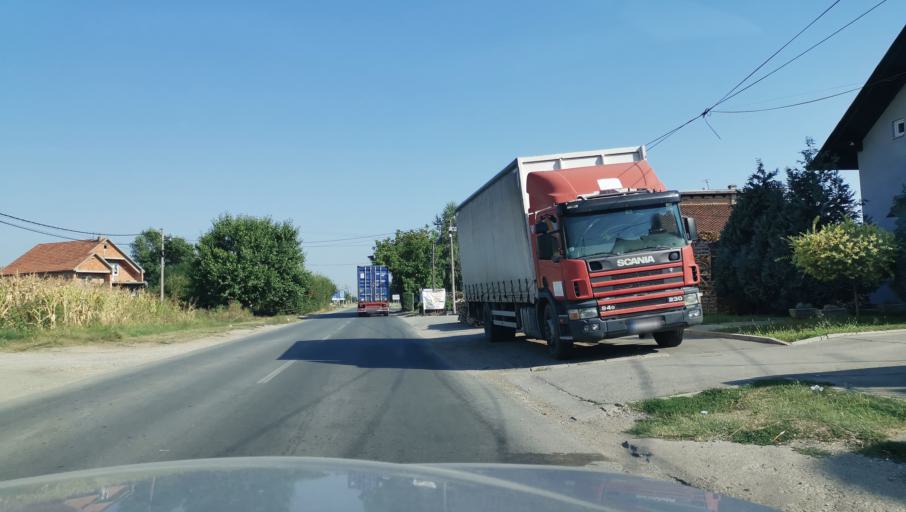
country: RS
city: Dobanovci
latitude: 44.8144
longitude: 20.2378
